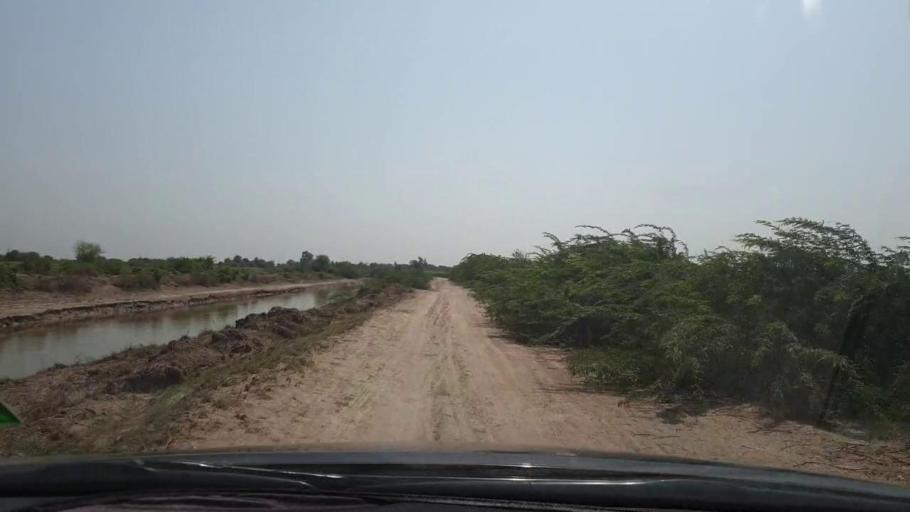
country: PK
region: Sindh
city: Tando Bago
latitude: 24.7872
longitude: 69.1203
